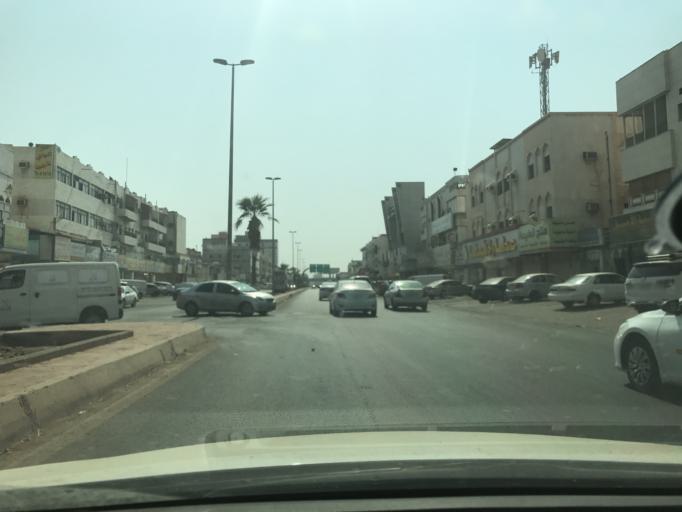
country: SA
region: Makkah
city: Jeddah
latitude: 21.6150
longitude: 39.1605
